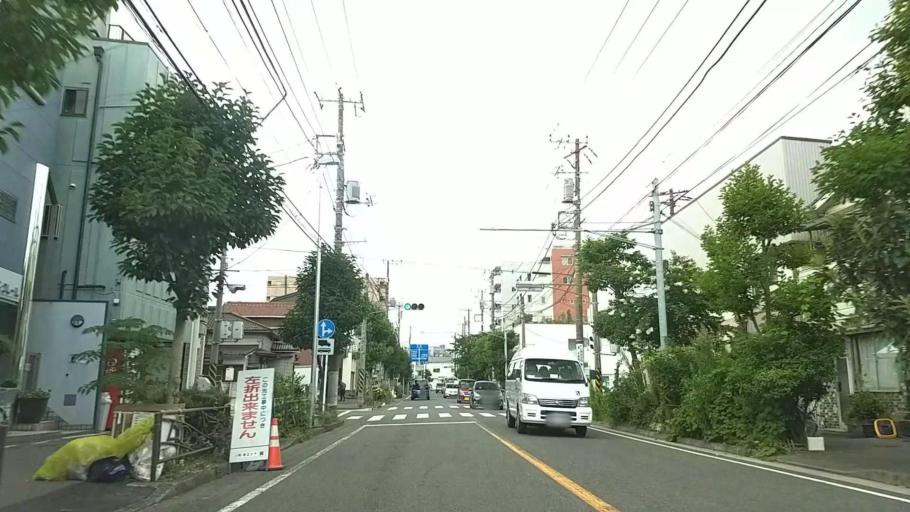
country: JP
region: Kanagawa
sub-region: Kawasaki-shi
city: Kawasaki
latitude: 35.5310
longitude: 139.7238
